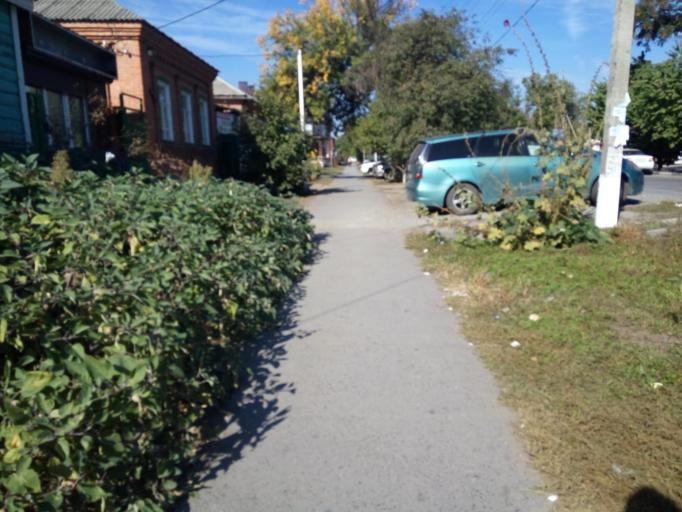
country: RU
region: Rostov
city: Bataysk
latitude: 47.1410
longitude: 39.7361
